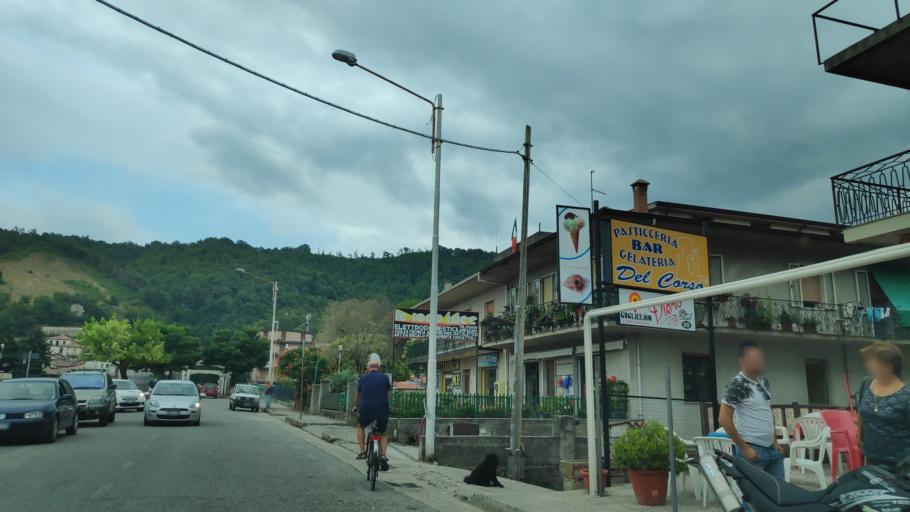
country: IT
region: Calabria
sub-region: Provincia di Catanzaro
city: Cardinale
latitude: 38.6446
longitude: 16.3852
